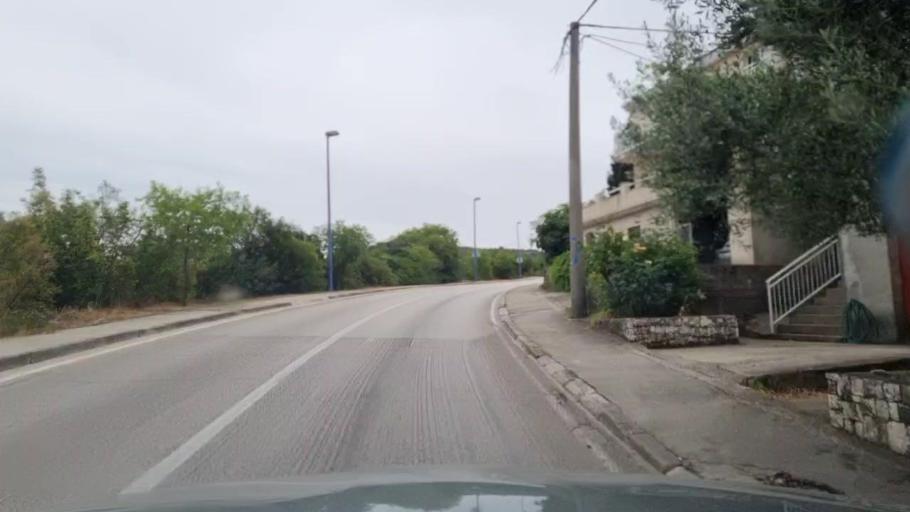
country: BA
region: Federation of Bosnia and Herzegovina
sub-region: Hercegovacko-Bosanski Kanton
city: Neum
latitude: 42.9267
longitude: 17.6187
